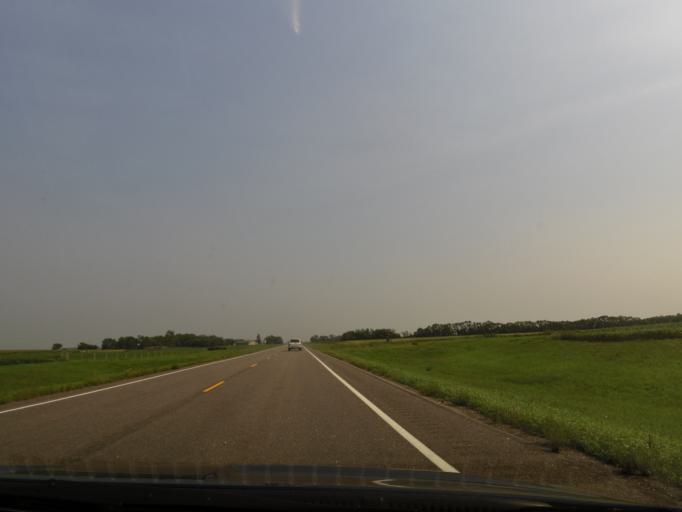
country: US
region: South Dakota
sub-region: Roberts County
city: Sisseton
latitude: 45.8483
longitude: -97.0847
